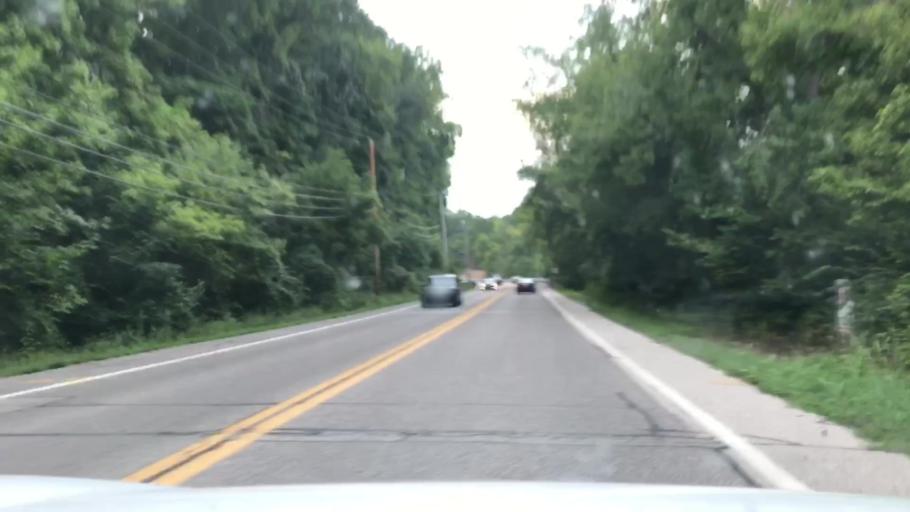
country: US
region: Missouri
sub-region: Saint Louis County
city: Chesterfield
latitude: 38.6546
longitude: -90.5928
